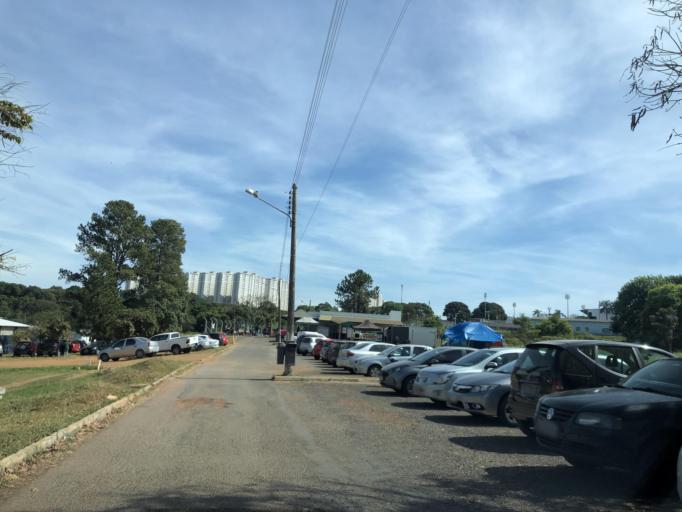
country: BR
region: Federal District
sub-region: Brasilia
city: Brasilia
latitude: -15.8168
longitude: -48.0723
